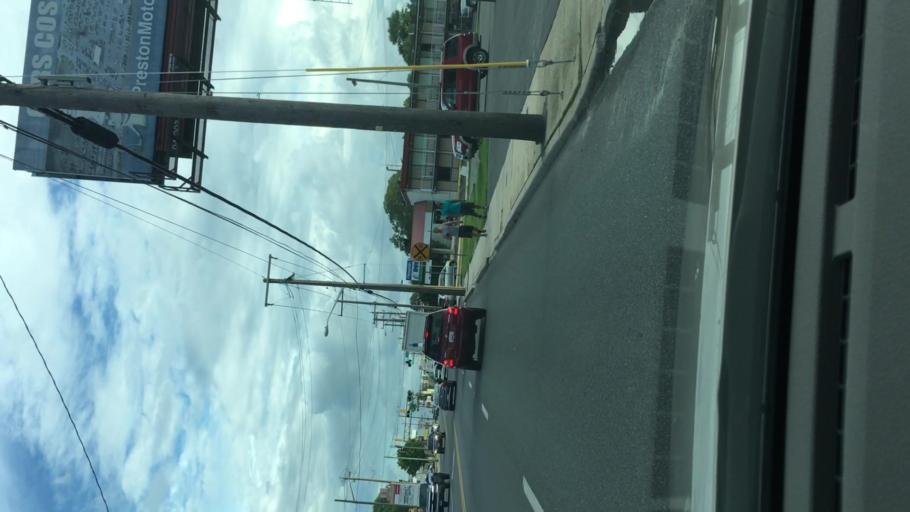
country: US
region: Maryland
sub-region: Wicomico County
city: Salisbury
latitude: 38.3732
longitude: -75.5933
